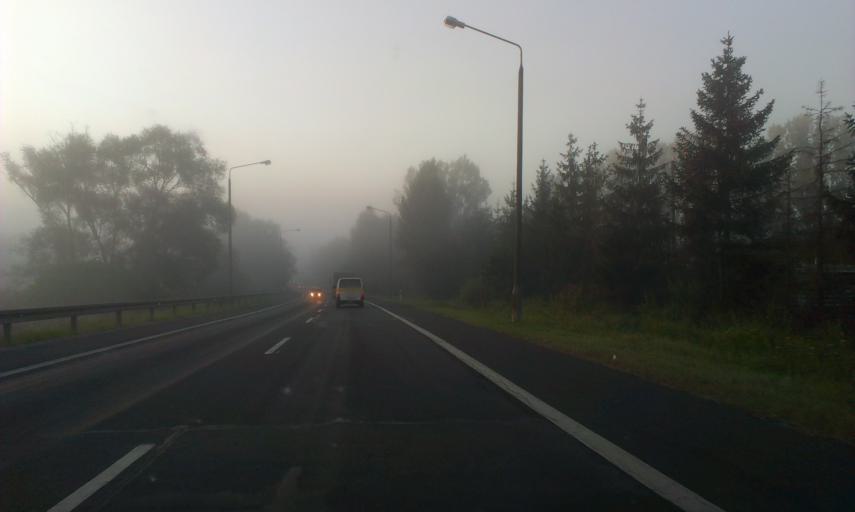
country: PL
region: Kujawsko-Pomorskie
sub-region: Powiat swiecki
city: Swiecie
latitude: 53.3949
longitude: 18.4025
